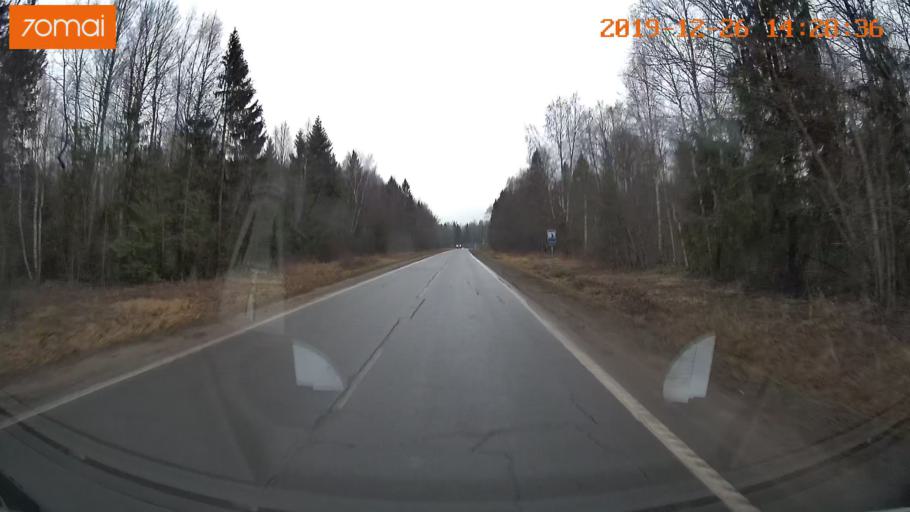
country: RU
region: Jaroslavl
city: Poshekhon'ye
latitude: 58.4737
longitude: 39.0511
